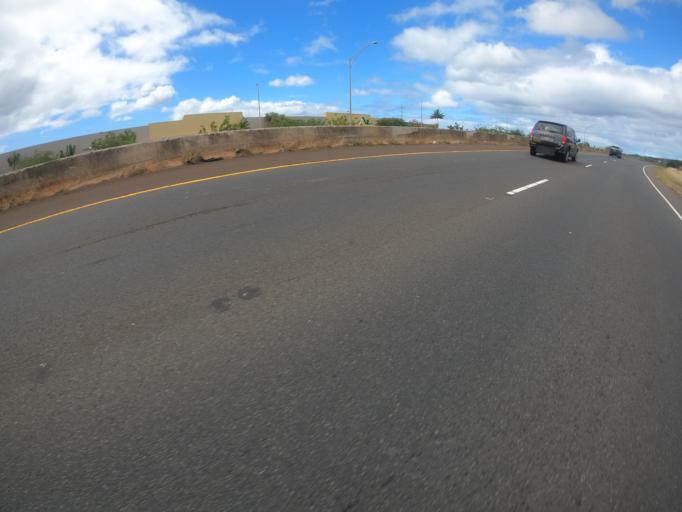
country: US
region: Hawaii
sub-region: Honolulu County
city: Makakilo City
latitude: 21.3327
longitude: -158.0918
